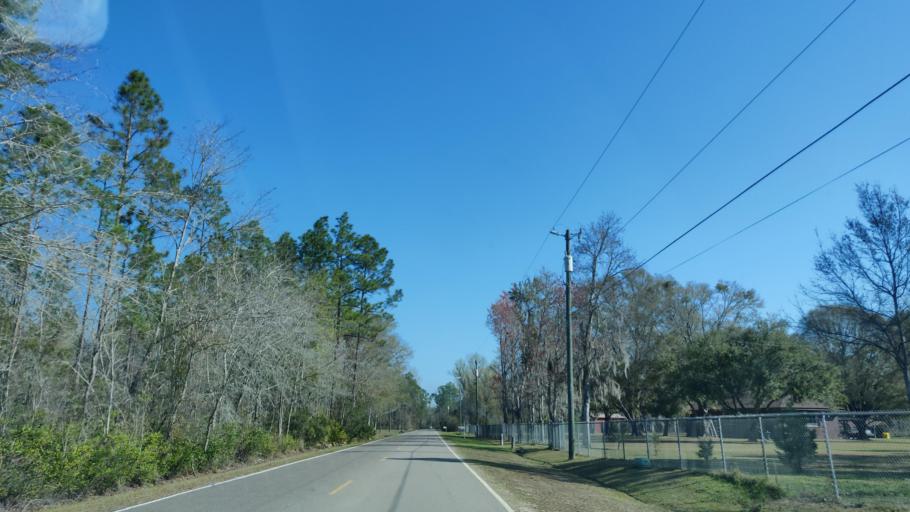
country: US
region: Florida
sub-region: Duval County
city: Baldwin
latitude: 30.1900
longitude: -81.9685
